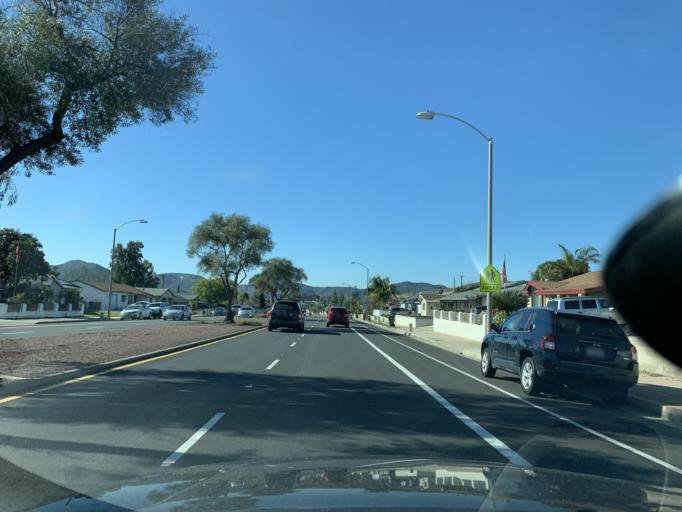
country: US
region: California
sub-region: San Diego County
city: Santee
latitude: 32.8526
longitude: -116.9961
